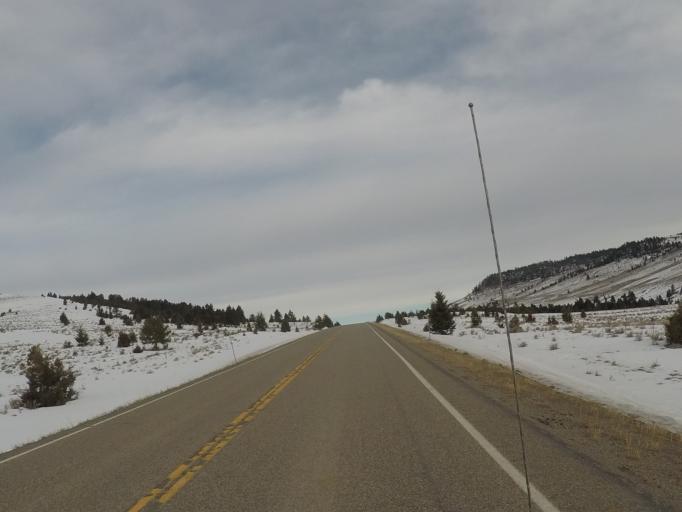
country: US
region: Montana
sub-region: Meagher County
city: White Sulphur Springs
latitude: 46.6406
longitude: -110.8752
